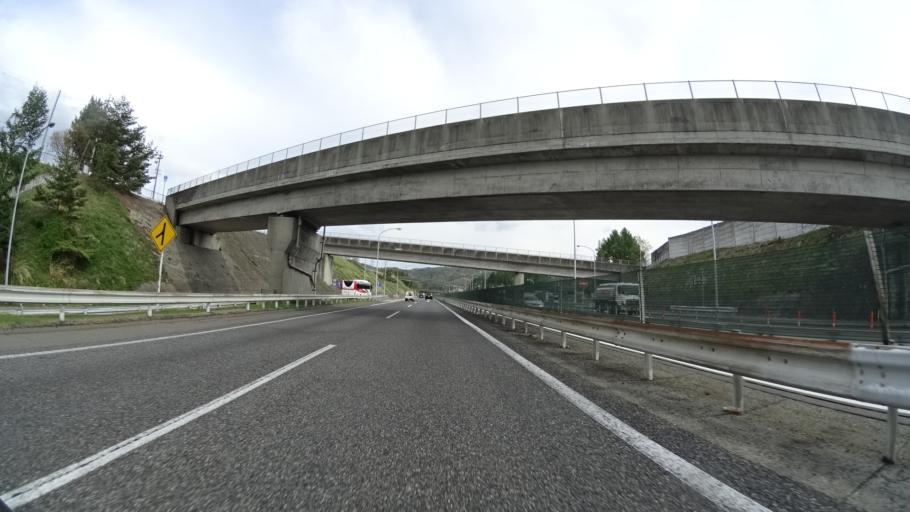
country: JP
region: Nagano
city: Shiojiri
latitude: 36.0986
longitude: 137.9961
